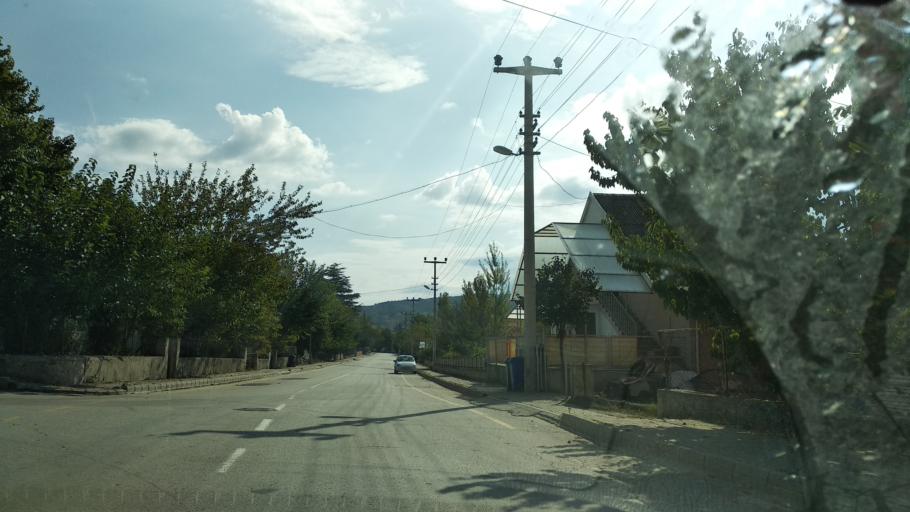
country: TR
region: Bolu
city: Seben
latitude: 40.4117
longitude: 31.5692
